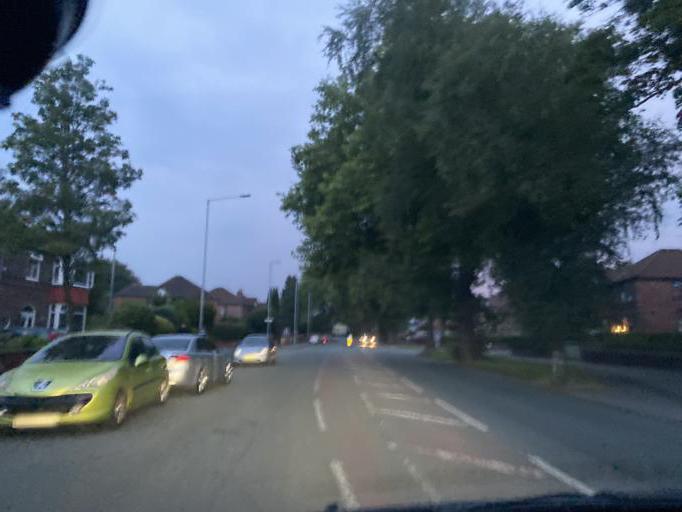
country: GB
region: England
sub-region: Manchester
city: Chorlton cum Hardy
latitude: 53.4497
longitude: -2.2742
